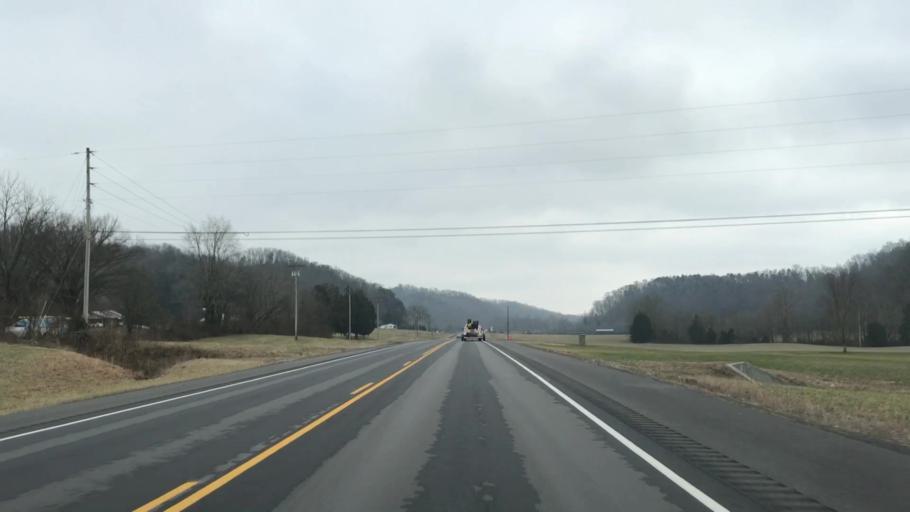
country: US
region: Kentucky
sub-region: Cumberland County
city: Burkesville
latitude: 36.8416
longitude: -85.3706
